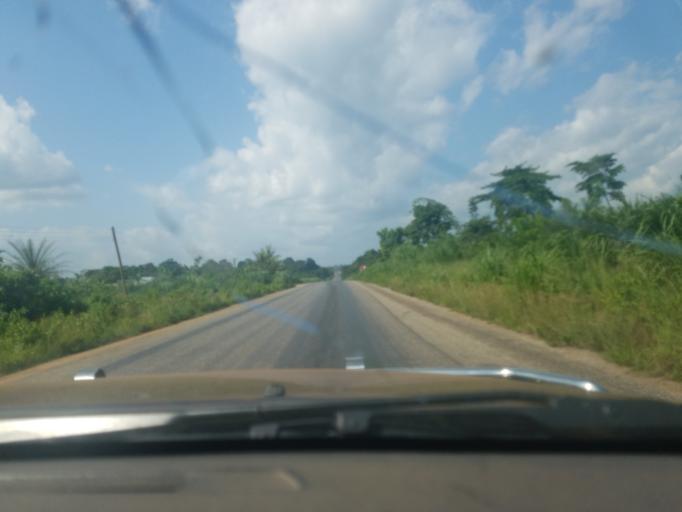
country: GH
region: Western
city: Bibiani
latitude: 6.8794
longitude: -2.4252
